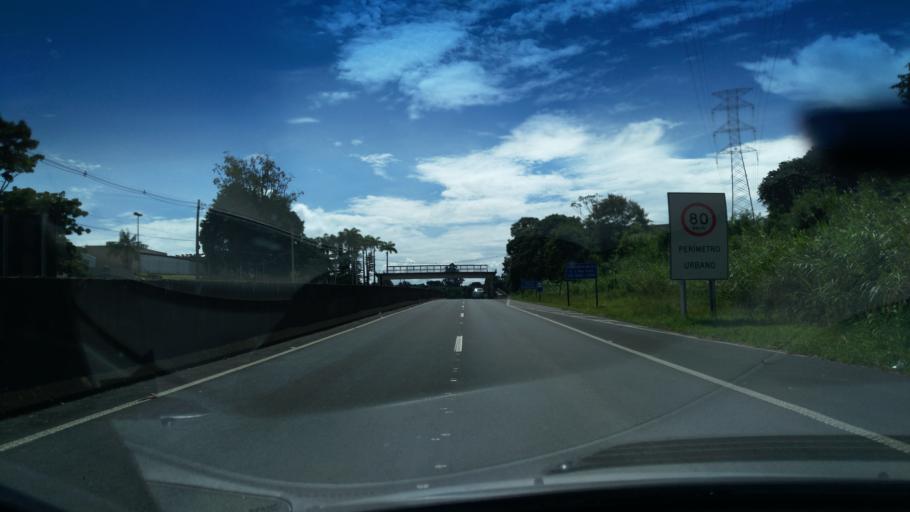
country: BR
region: Sao Paulo
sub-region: Santo Antonio Do Jardim
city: Espirito Santo do Pinhal
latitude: -22.1878
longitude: -46.7662
